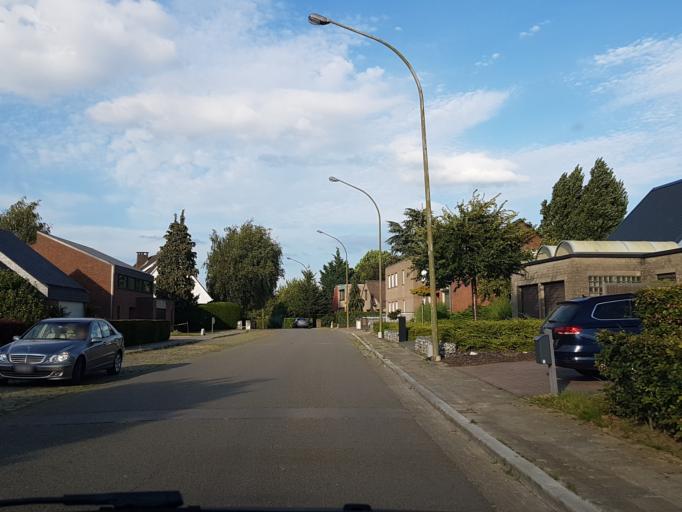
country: BE
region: Flanders
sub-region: Provincie Vlaams-Brabant
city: Leuven
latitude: 50.8887
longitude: 4.6879
